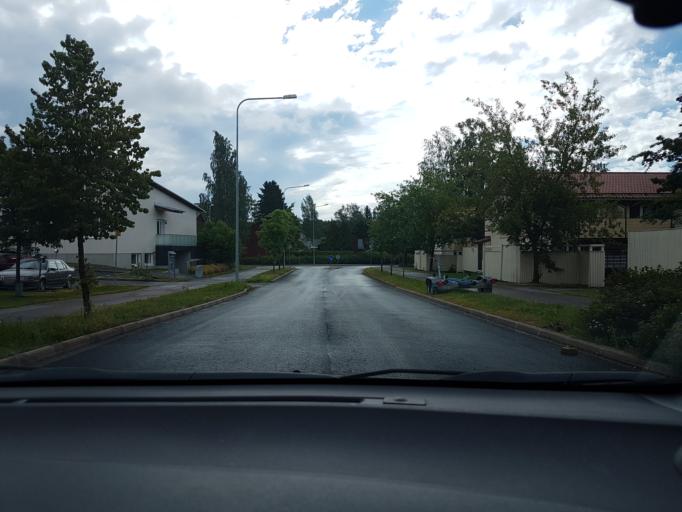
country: FI
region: Uusimaa
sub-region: Helsinki
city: Vantaa
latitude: 60.2196
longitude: 25.1153
